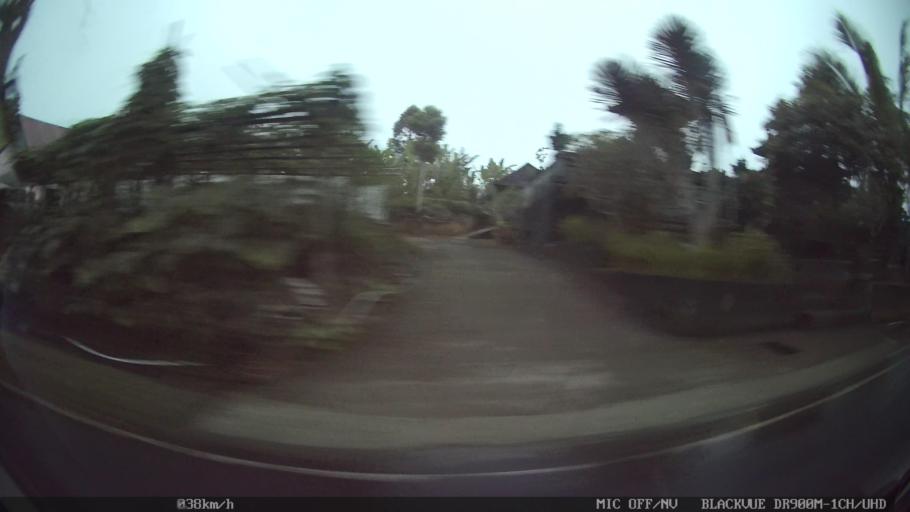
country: ID
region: Bali
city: Banjar Taro Kelod
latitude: -8.3165
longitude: 115.2997
